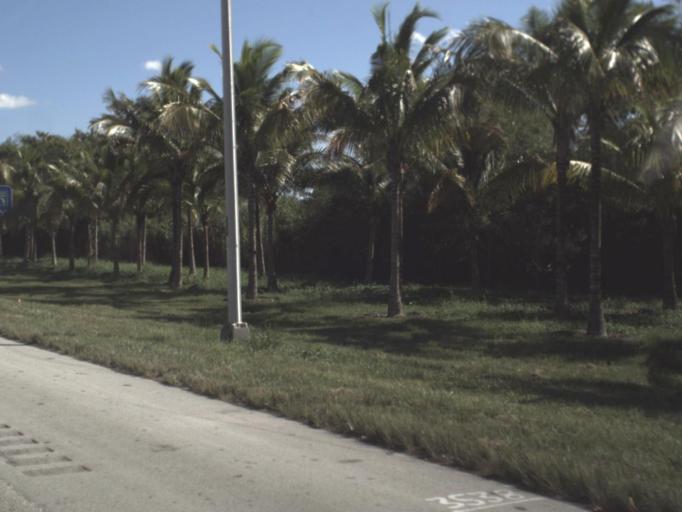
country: US
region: Florida
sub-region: Miami-Dade County
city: Florida City
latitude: 25.4562
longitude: -80.4711
